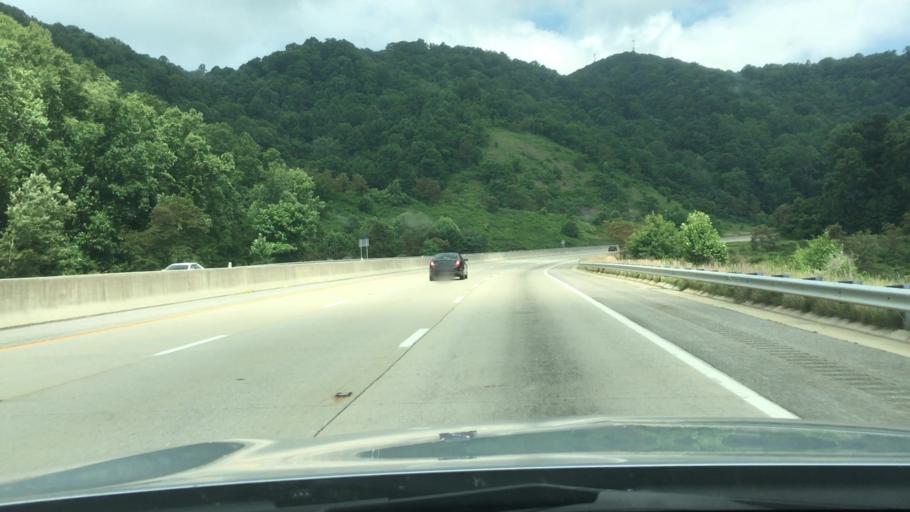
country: US
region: North Carolina
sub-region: Madison County
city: Mars Hill
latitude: 35.8784
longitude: -82.5476
